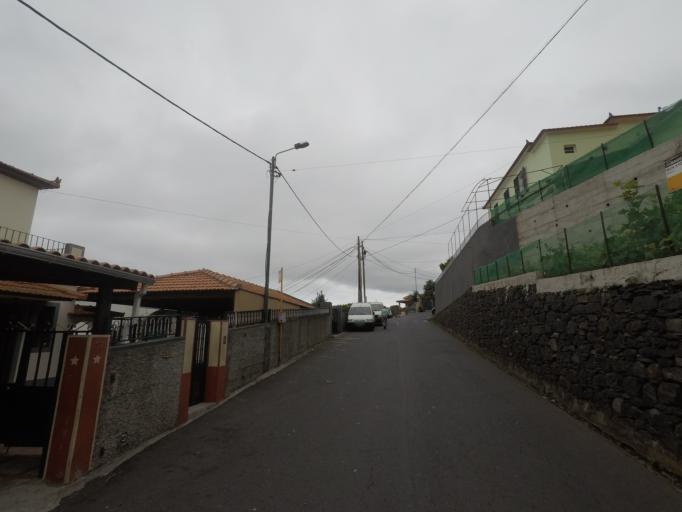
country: PT
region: Madeira
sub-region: Funchal
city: Nossa Senhora do Monte
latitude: 32.6756
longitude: -16.9419
